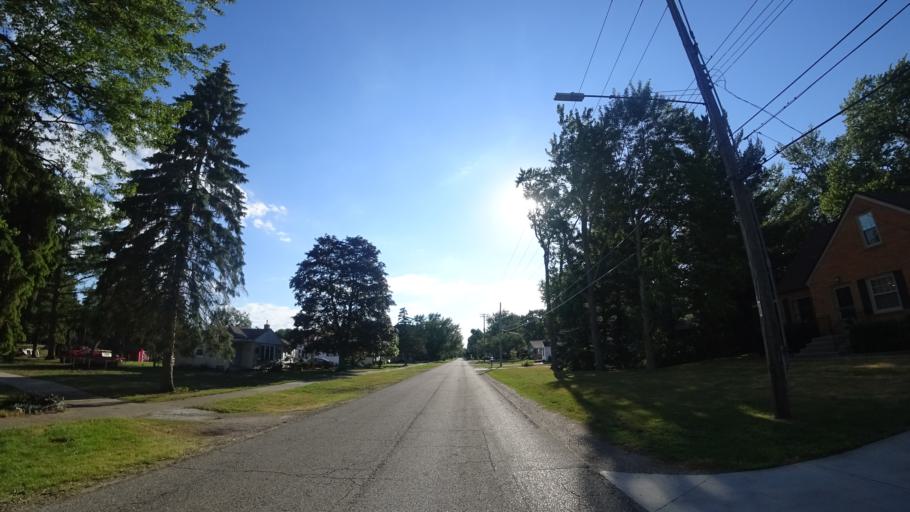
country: US
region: Michigan
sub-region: Ottawa County
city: Holland
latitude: 42.7654
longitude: -86.1078
